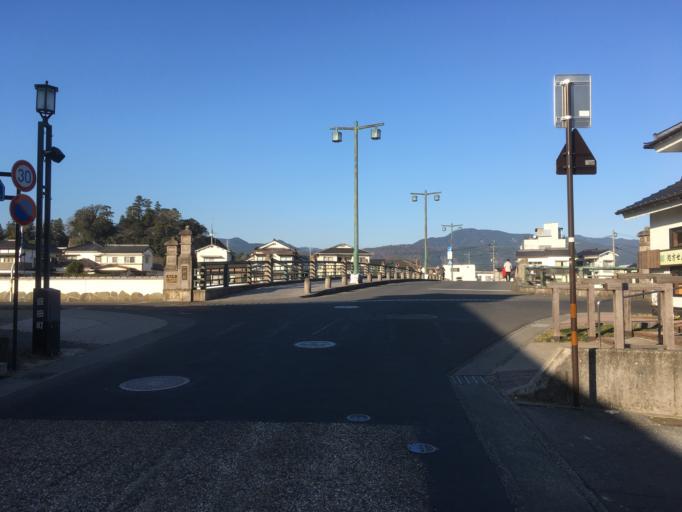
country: JP
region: Oita
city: Hita
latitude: 33.3289
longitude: 130.9376
